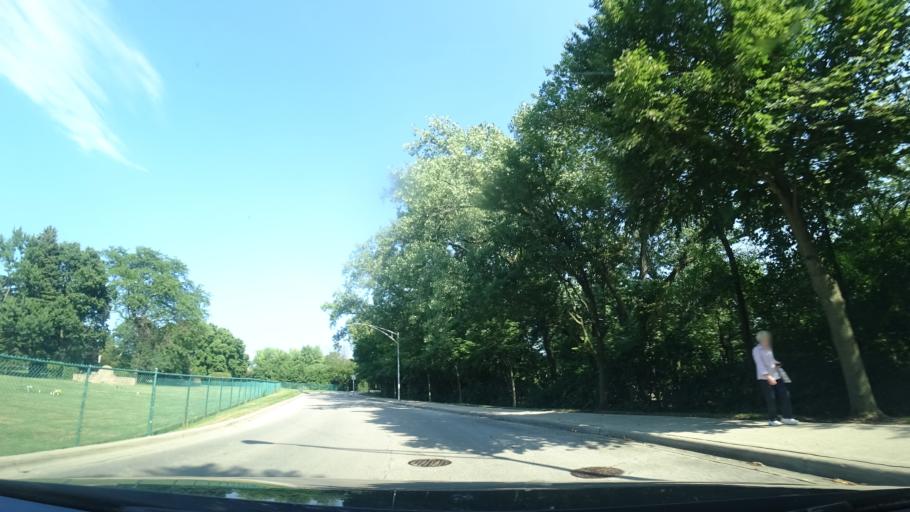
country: US
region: Illinois
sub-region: Cook County
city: Lincolnwood
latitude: 41.9761
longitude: -87.7329
